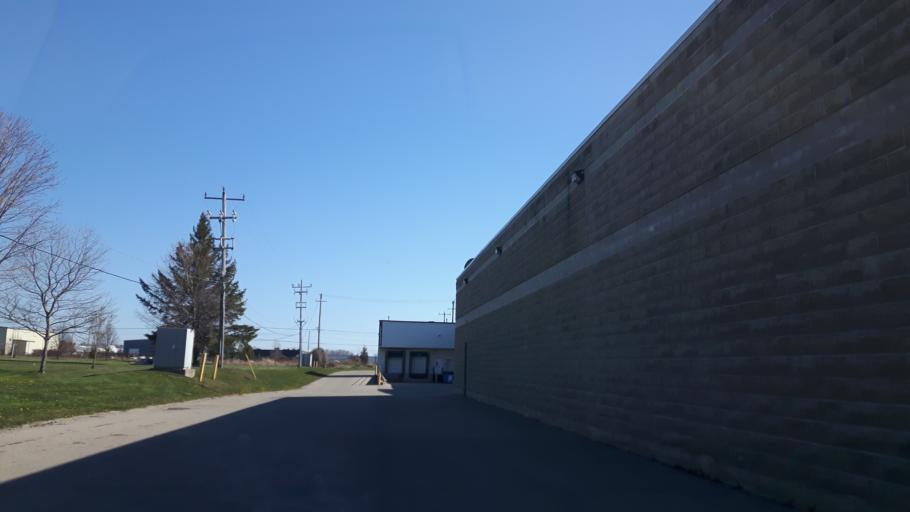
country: CA
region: Ontario
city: Goderich
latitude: 43.7294
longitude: -81.7030
